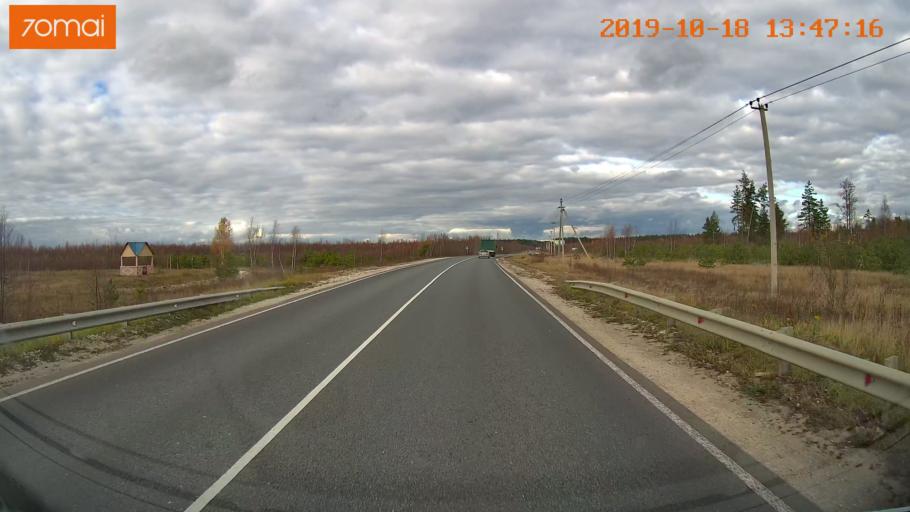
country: RU
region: Rjazan
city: Solotcha
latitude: 54.9721
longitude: 39.9512
